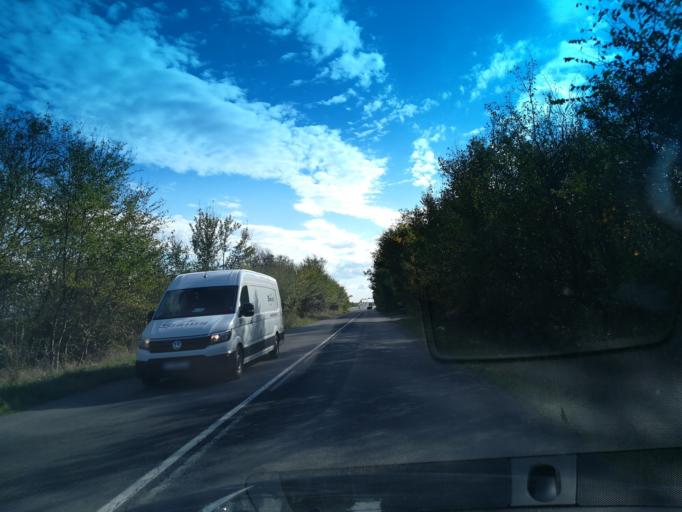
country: BG
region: Stara Zagora
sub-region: Obshtina Stara Zagora
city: Stara Zagora
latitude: 42.3479
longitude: 25.6595
